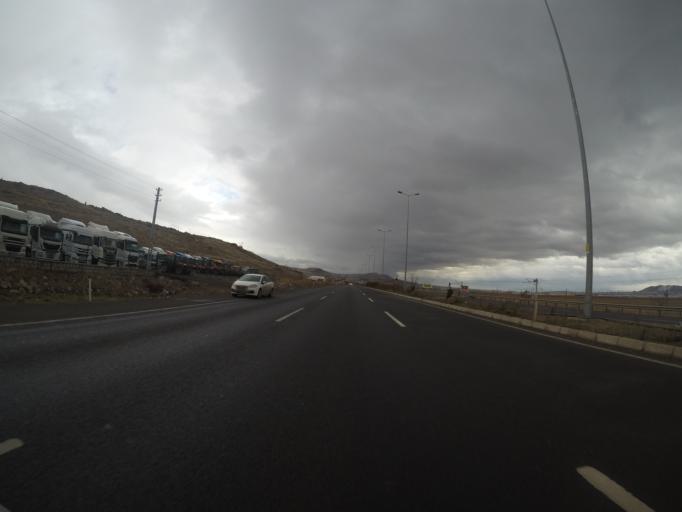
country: TR
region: Kayseri
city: Melikgazi
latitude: 38.7426
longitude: 35.2983
